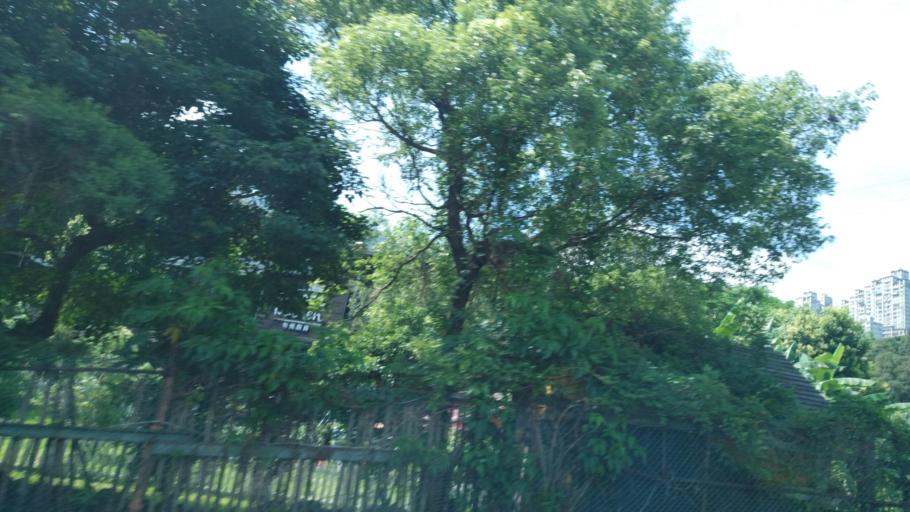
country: TW
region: Taipei
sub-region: Taipei
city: Banqiao
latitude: 24.9485
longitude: 121.5049
